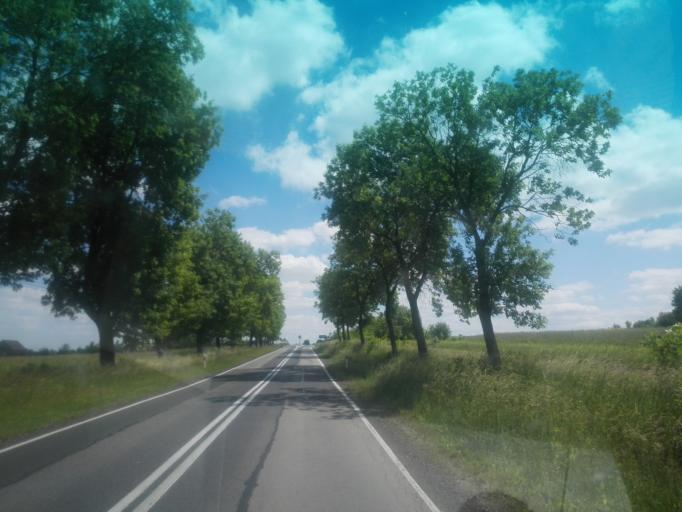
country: PL
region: Silesian Voivodeship
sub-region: Powiat czestochowski
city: Potok Zloty
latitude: 50.7318
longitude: 19.4016
